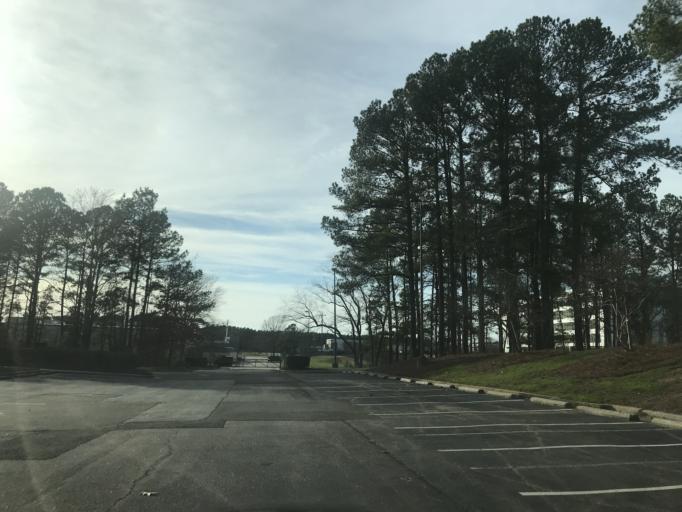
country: US
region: North Carolina
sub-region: Wake County
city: Morrisville
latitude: 35.8751
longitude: -78.8472
